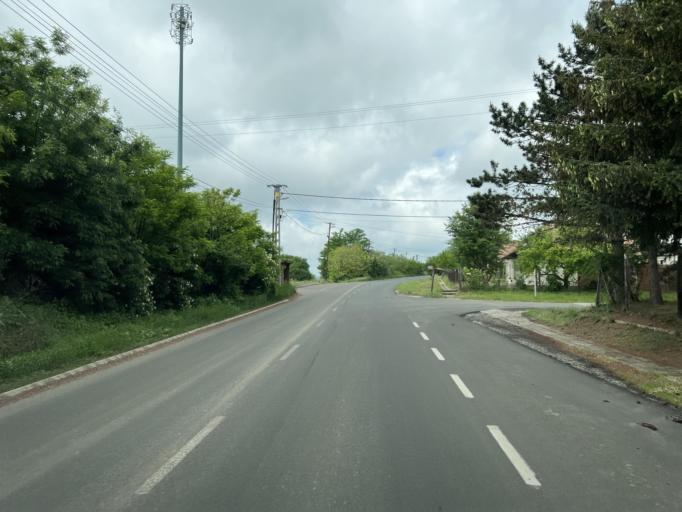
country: HU
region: Pest
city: Kartal
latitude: 47.7243
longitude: 19.5398
